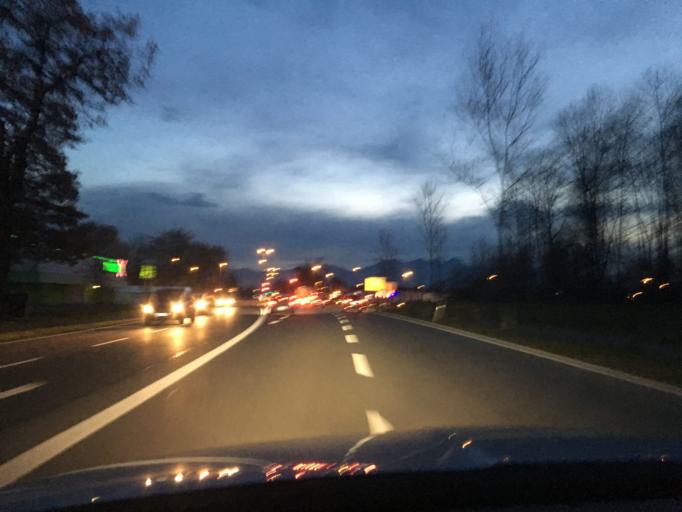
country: DE
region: Bavaria
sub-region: Upper Bavaria
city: Rosenheim
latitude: 47.8412
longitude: 12.1222
